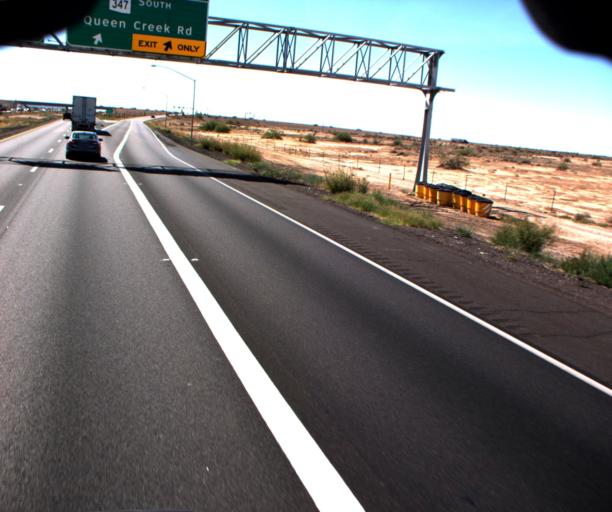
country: US
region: Arizona
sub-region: Maricopa County
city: Sun Lakes
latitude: 33.2604
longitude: -111.9522
